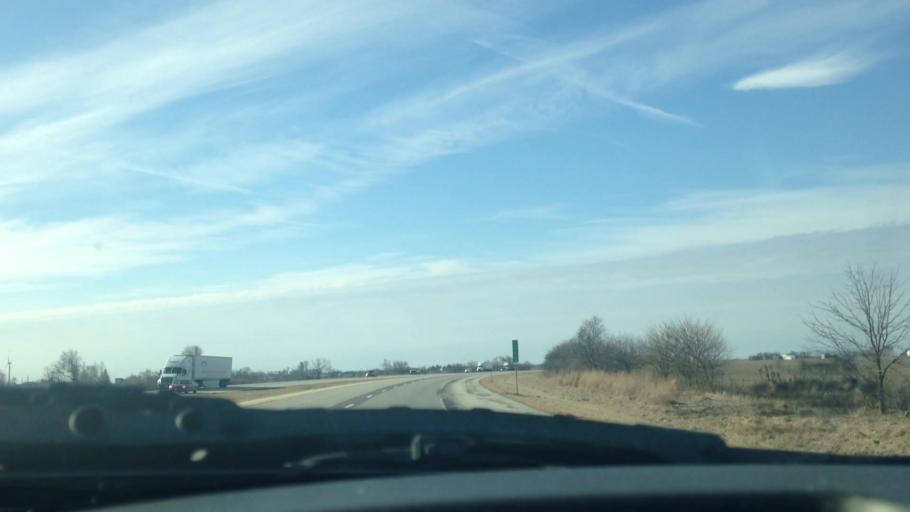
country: US
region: Illinois
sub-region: Ford County
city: Paxton
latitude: 40.5087
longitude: -88.0848
